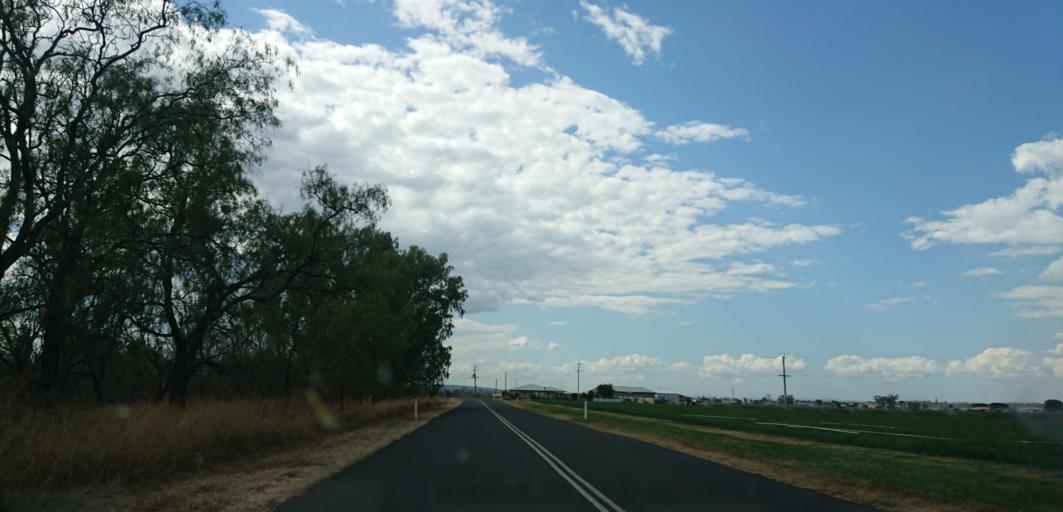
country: AU
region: Queensland
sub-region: Lockyer Valley
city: Gatton
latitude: -27.5941
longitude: 152.2255
